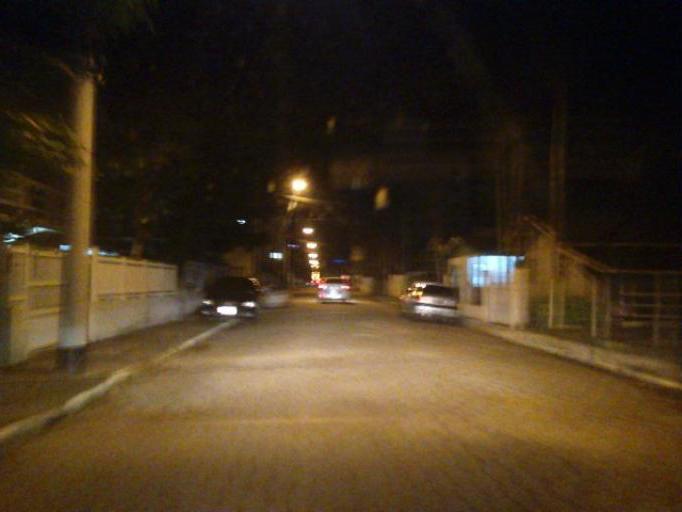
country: BR
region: Santa Catarina
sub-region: Itapema
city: Itapema
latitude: -27.1201
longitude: -48.6114
